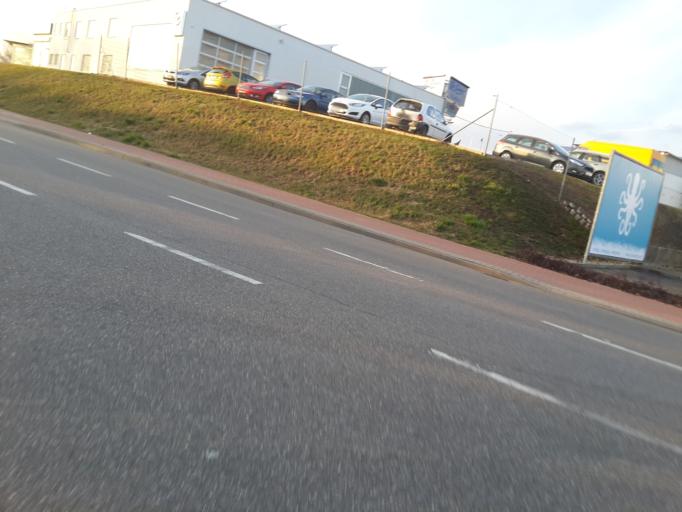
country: DE
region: Baden-Wuerttemberg
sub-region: Regierungsbezirk Stuttgart
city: Untereisesheim
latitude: 49.2132
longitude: 9.2154
